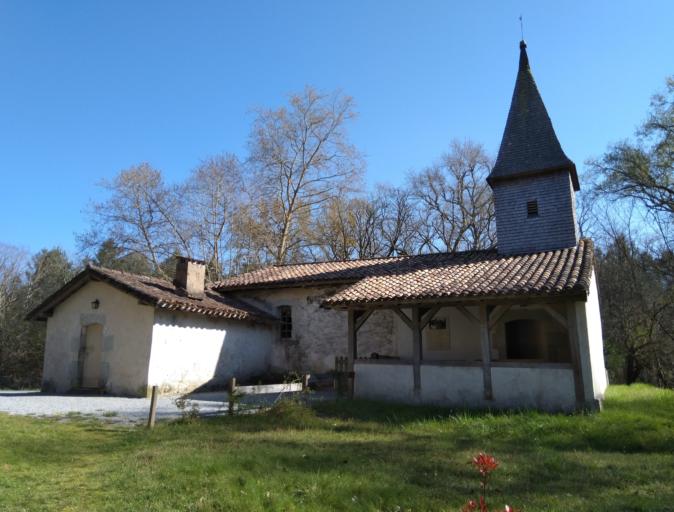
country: FR
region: Aquitaine
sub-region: Departement des Landes
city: Saint-Geours-de-Maremne
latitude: 43.7090
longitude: -1.1888
